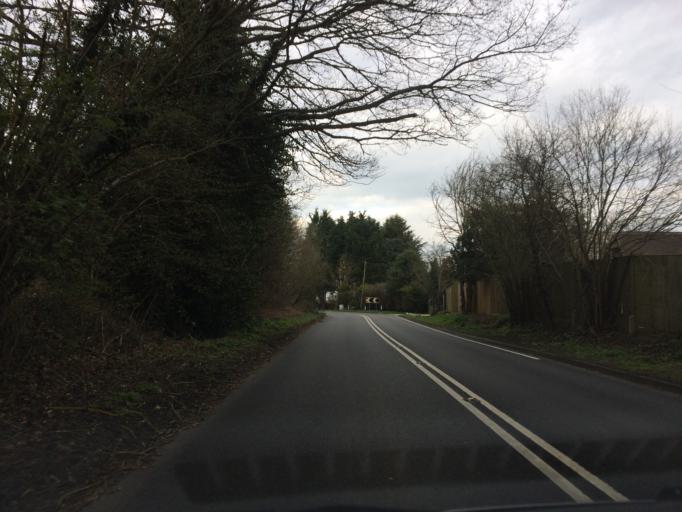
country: GB
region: England
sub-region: Surrey
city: Woking
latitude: 51.3487
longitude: -0.5690
